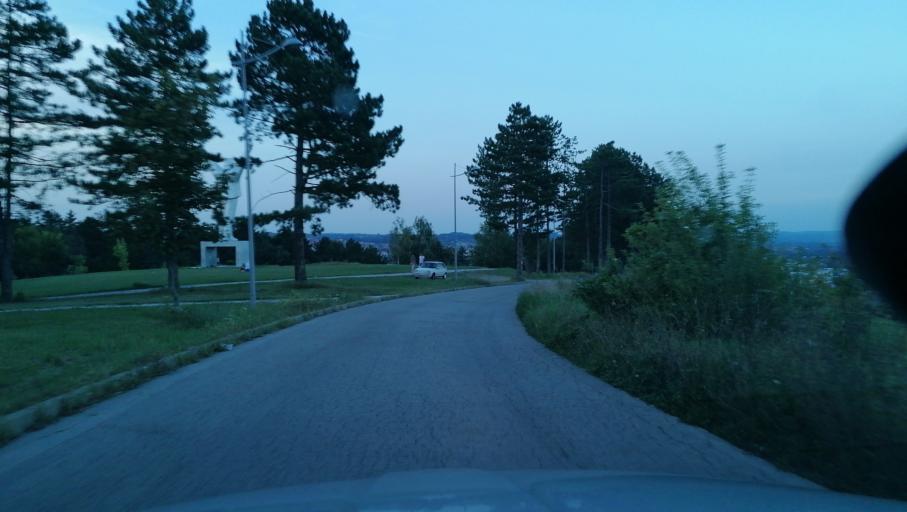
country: RS
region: Central Serbia
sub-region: Kolubarski Okrug
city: Valjevo
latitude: 44.2630
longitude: 19.8803
